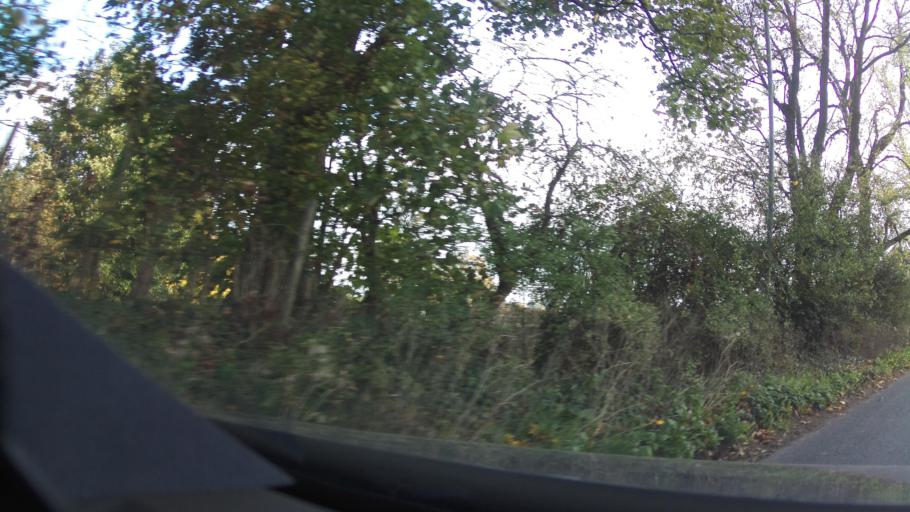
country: GB
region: England
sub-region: Wiltshire
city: Bradford-on-Avon
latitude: 51.3585
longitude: -2.2545
